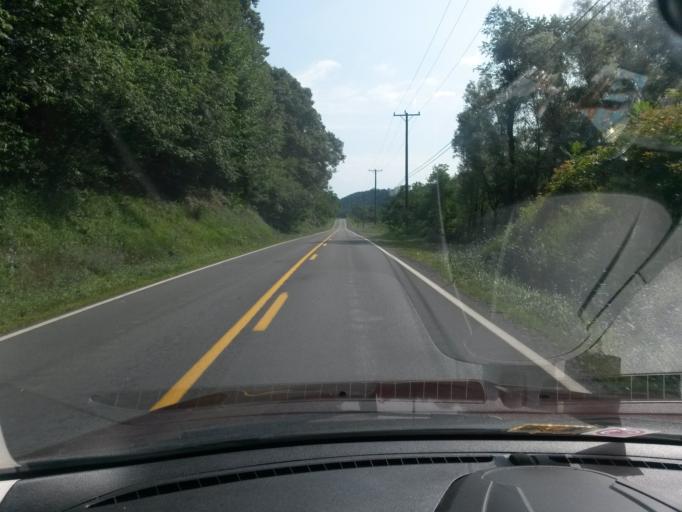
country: US
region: Virginia
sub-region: Shenandoah County
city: Basye
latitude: 38.9819
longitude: -78.7885
